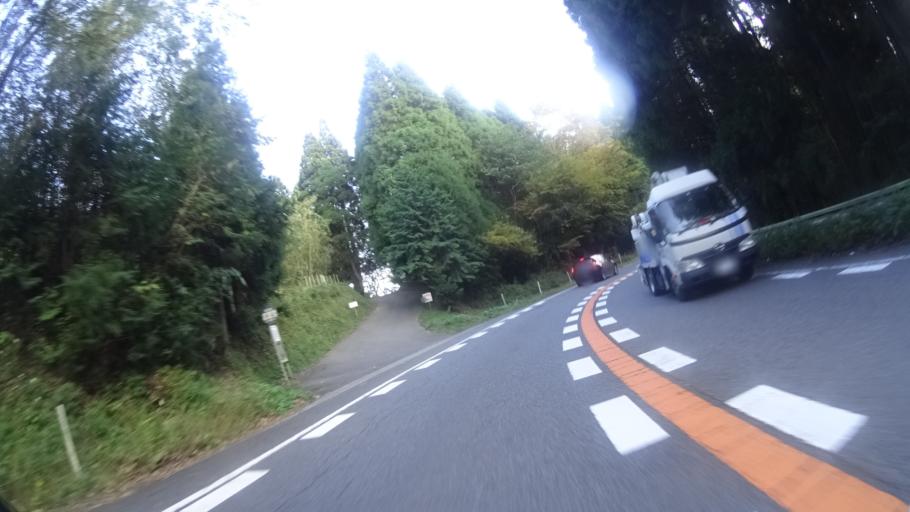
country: JP
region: Oita
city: Beppu
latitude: 33.2700
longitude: 131.4301
